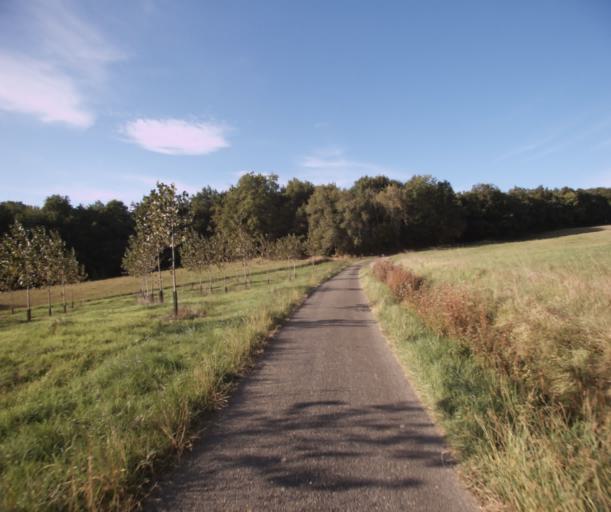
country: FR
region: Midi-Pyrenees
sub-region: Departement du Gers
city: Eauze
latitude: 43.8410
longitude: 0.0332
